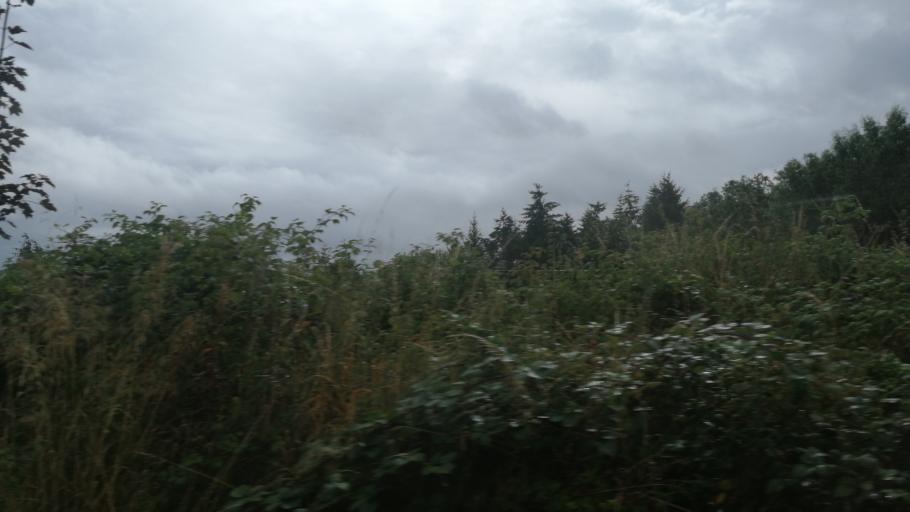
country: GB
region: Scotland
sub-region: Highland
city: Evanton
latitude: 57.6409
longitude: -4.3519
